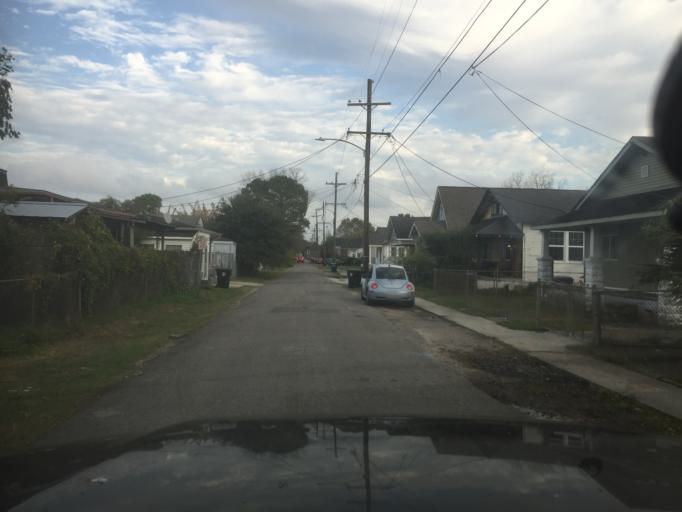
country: US
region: Louisiana
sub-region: Orleans Parish
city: New Orleans
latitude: 29.9867
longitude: -90.0805
